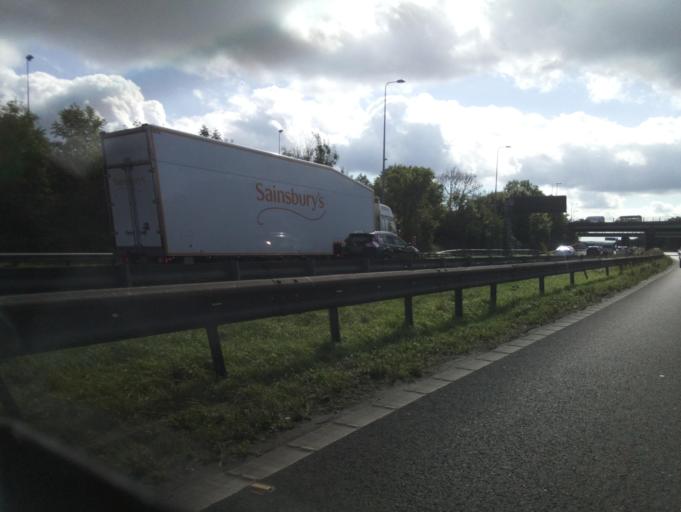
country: GB
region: England
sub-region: Borough of Wigan
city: Shevington
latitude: 53.5914
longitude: -2.6944
